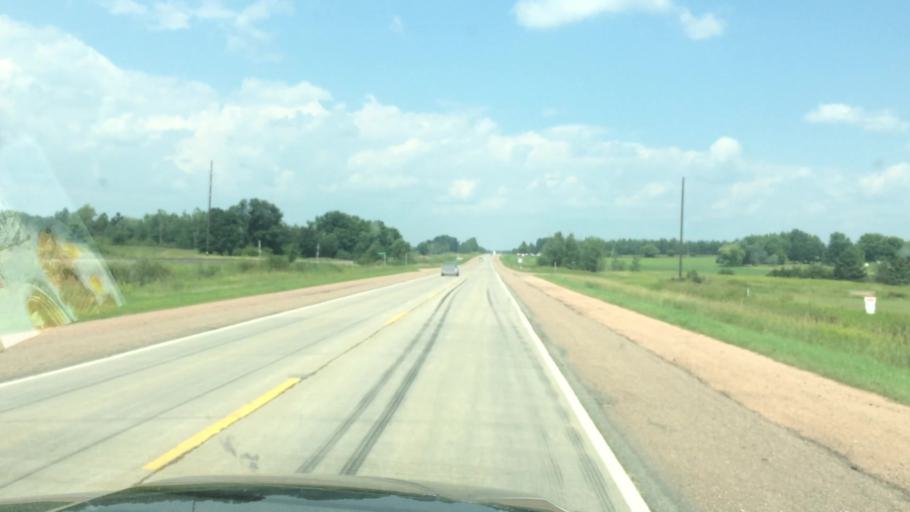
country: US
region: Wisconsin
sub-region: Clark County
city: Colby
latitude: 44.8721
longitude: -90.3157
